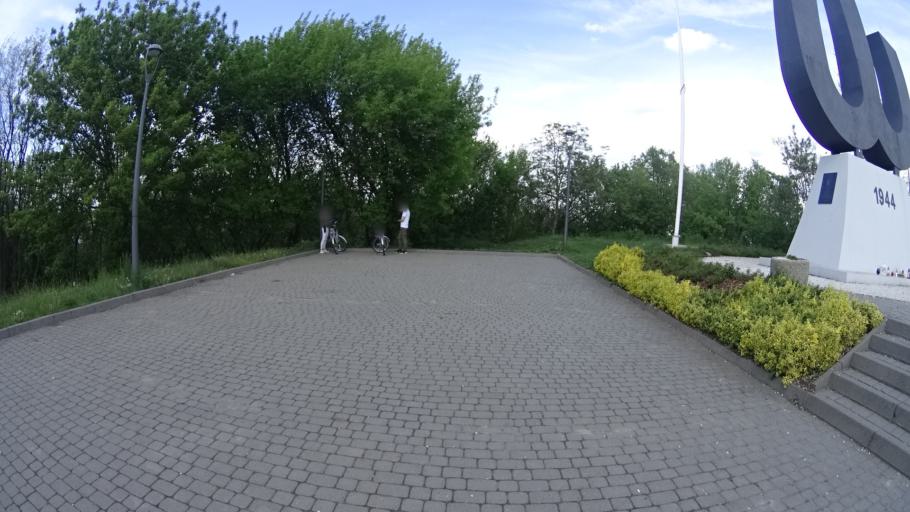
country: PL
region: Masovian Voivodeship
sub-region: Warszawa
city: Mokotow
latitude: 52.2111
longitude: 21.0560
